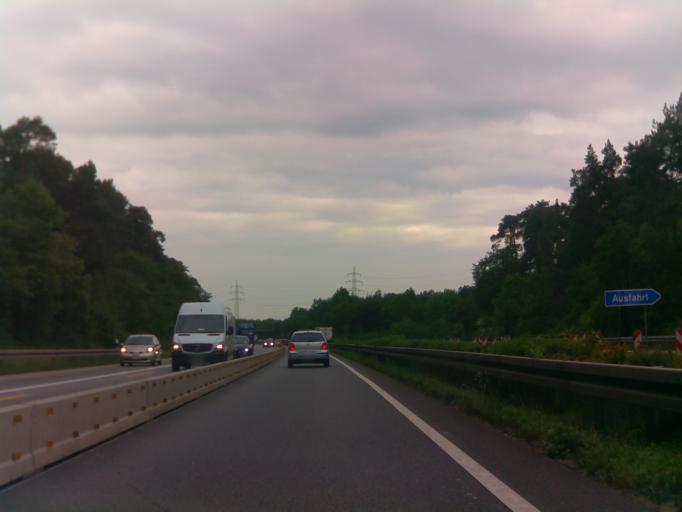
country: DE
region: Hesse
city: Raunheim
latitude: 49.9950
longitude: 8.4712
